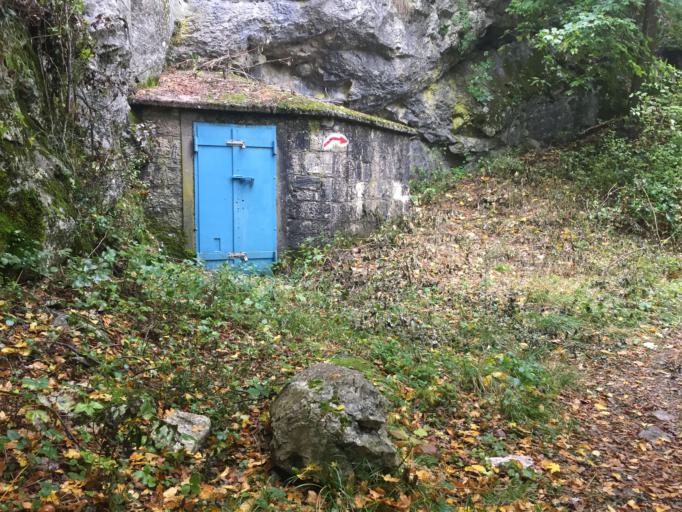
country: HR
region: Istarska
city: Buzet
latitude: 45.4565
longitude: 14.0135
